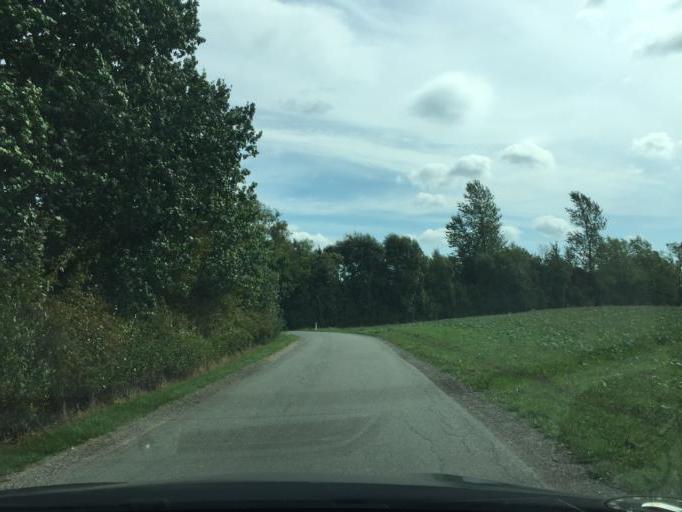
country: DK
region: South Denmark
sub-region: Assens Kommune
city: Tommerup
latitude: 55.3949
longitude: 10.2452
